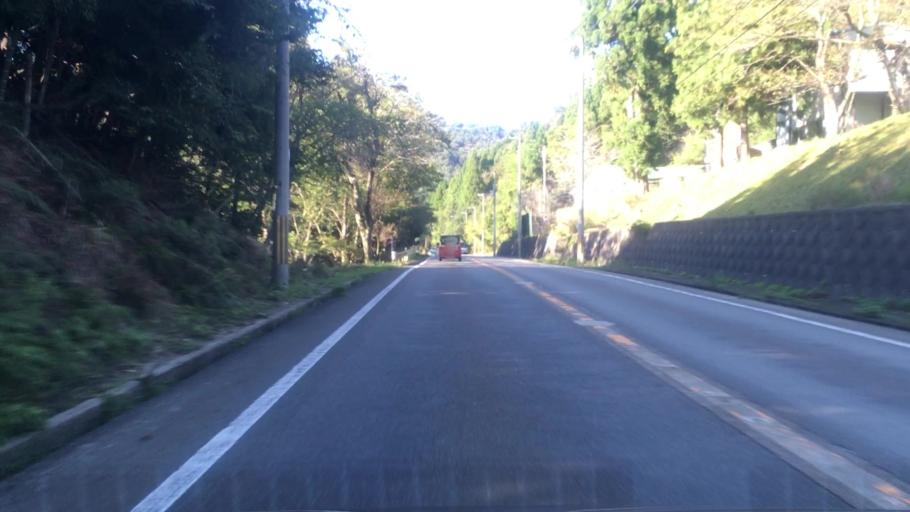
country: JP
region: Hyogo
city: Toyooka
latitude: 35.5674
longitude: 134.8527
